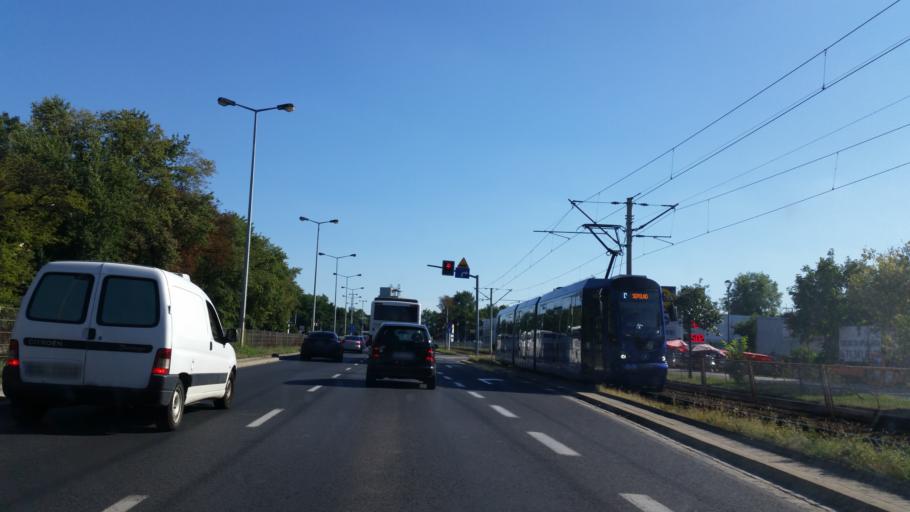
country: PL
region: Lower Silesian Voivodeship
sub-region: Powiat wroclawski
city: Wroclaw
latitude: 51.0776
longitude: 17.0074
